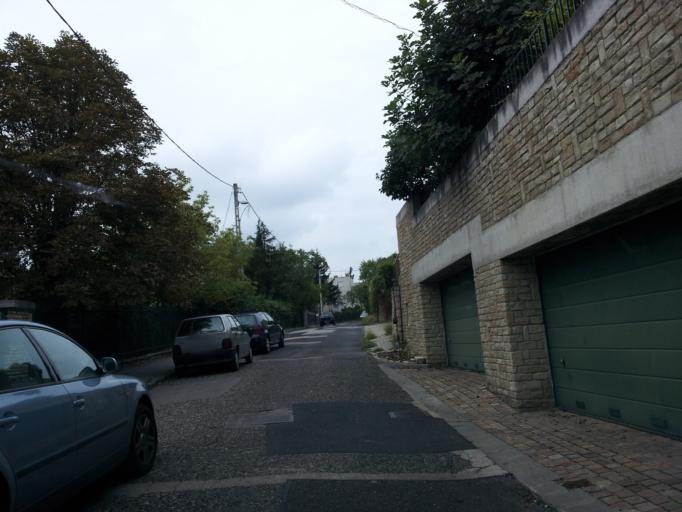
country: HU
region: Budapest
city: Budapest II. keruelet
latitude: 47.5201
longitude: 19.0203
